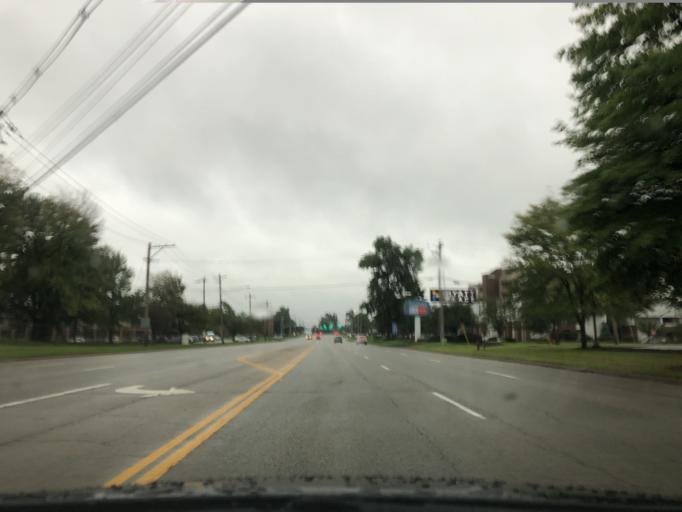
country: US
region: Ohio
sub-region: Hamilton County
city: Highpoint
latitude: 39.2765
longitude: -84.3741
